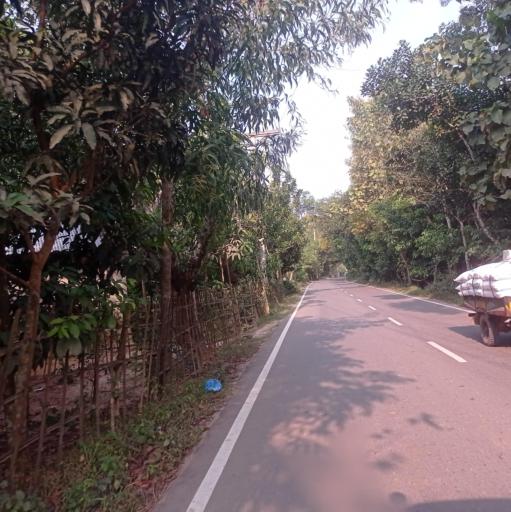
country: BD
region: Dhaka
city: Bhairab Bazar
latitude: 24.0715
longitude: 90.8429
